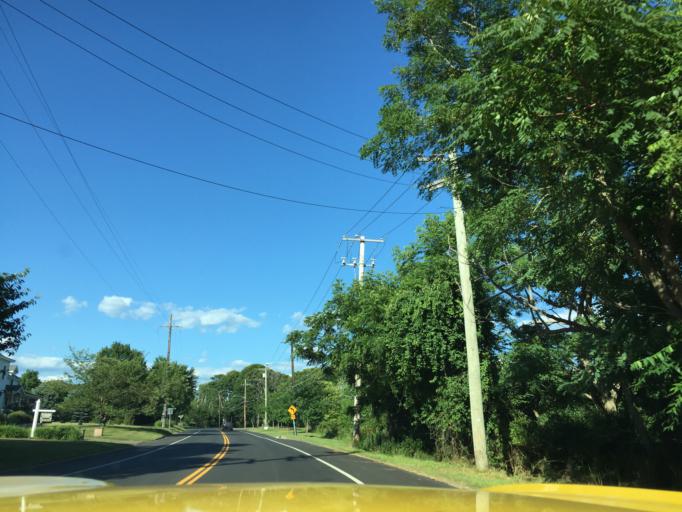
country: US
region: New York
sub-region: Suffolk County
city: Greenport
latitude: 41.1200
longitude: -72.3499
